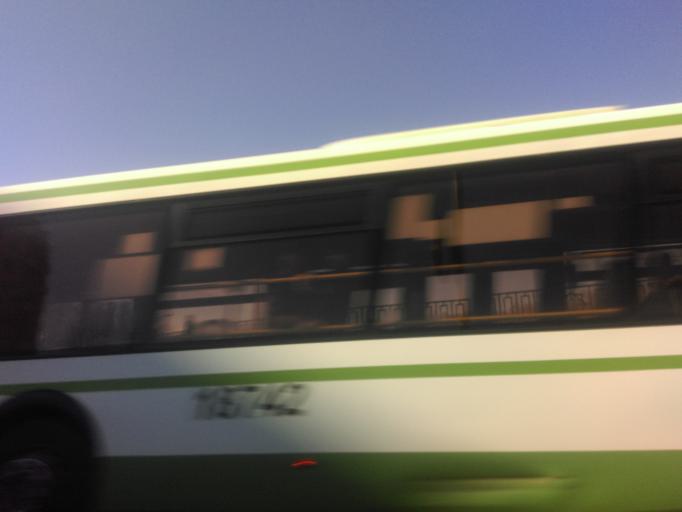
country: RU
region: Moskovskaya
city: Mosrentgen
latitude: 55.6350
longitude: 37.4728
